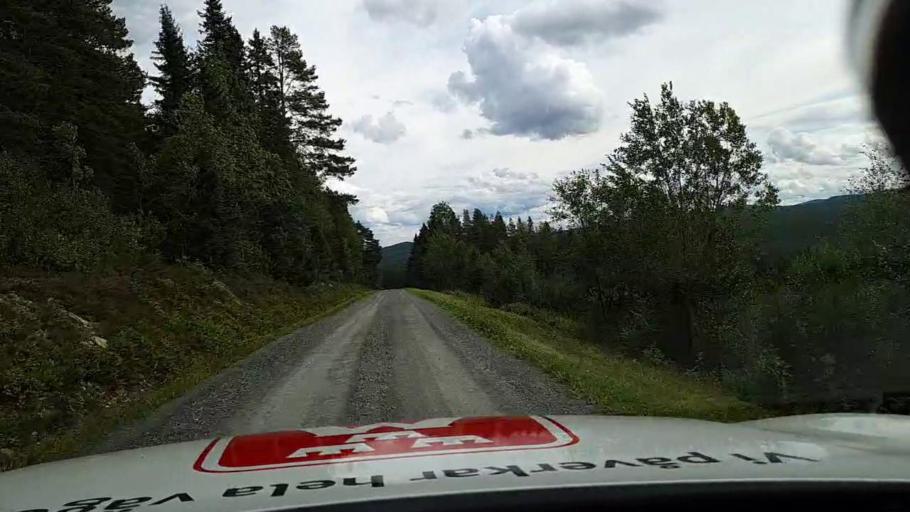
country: SE
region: Jaemtland
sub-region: Krokoms Kommun
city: Valla
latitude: 63.5832
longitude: 13.9735
